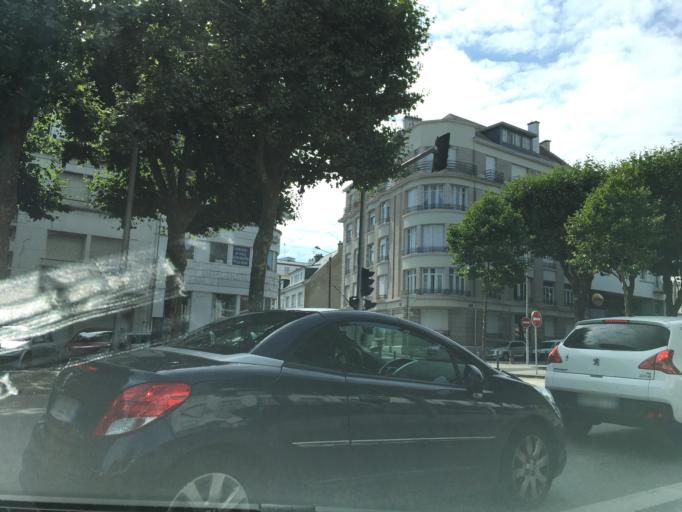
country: FR
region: Brittany
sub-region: Departement du Morbihan
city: Lorient
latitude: 47.7537
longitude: -3.3623
